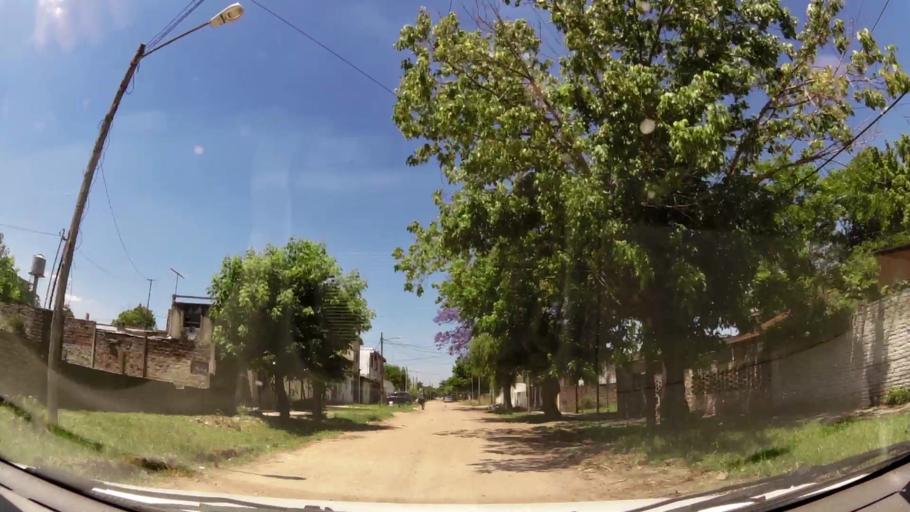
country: AR
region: Buenos Aires
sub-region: Partido de Merlo
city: Merlo
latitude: -34.6448
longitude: -58.7170
